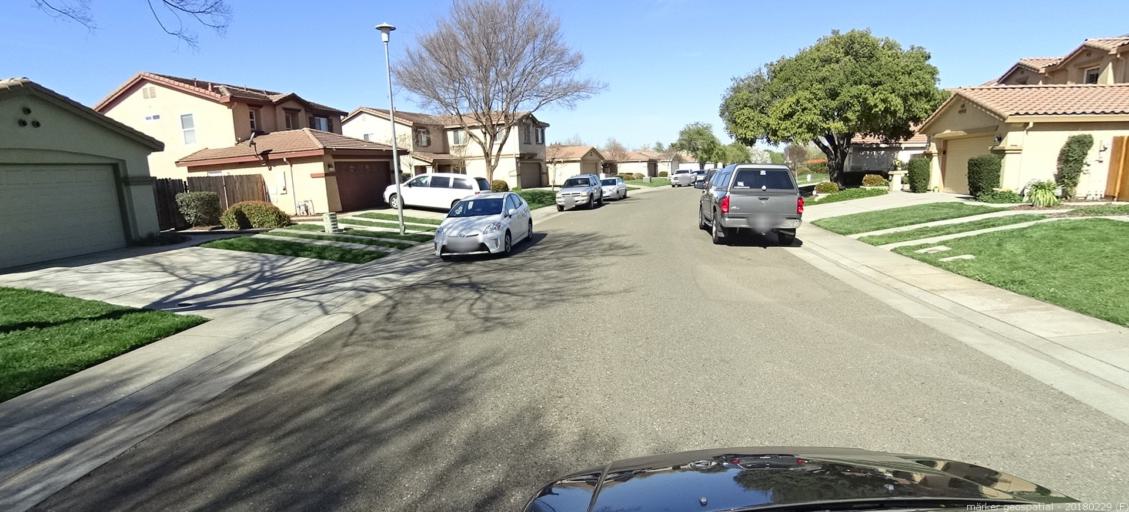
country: US
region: California
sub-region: Sacramento County
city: Rancho Cordova
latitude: 38.5419
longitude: -121.2827
